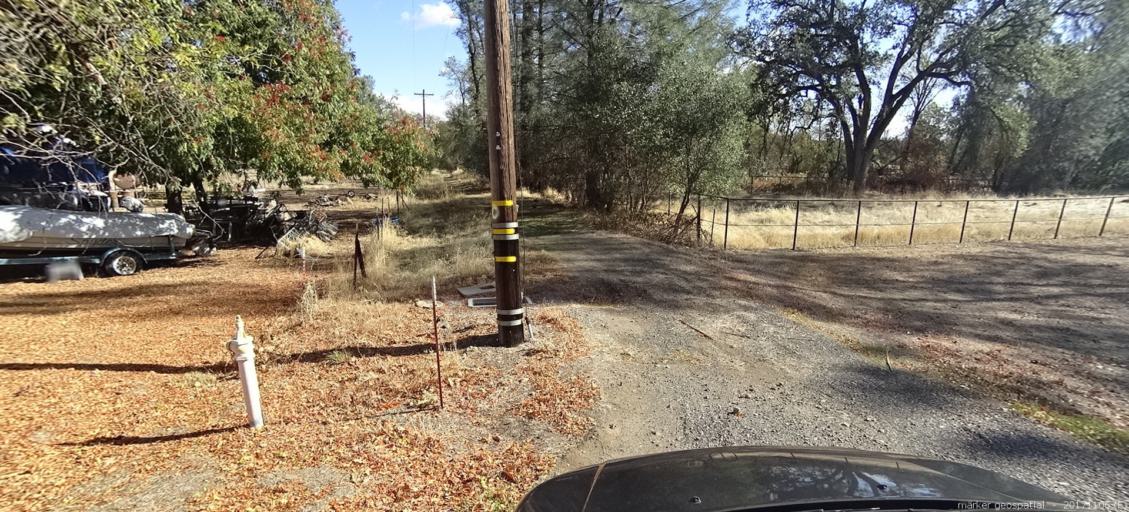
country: US
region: California
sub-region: Shasta County
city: Palo Cedro
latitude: 40.5710
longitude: -122.2236
